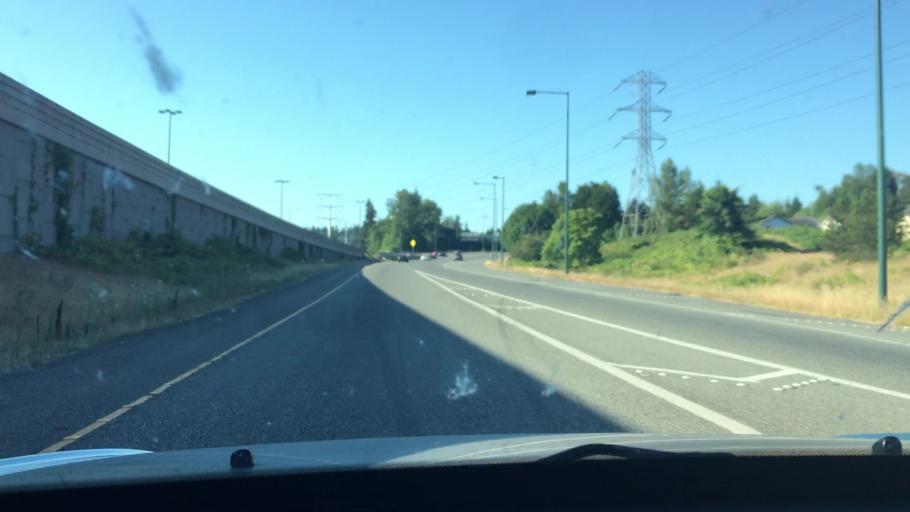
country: US
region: Washington
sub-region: King County
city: Newport
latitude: 47.5783
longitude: -122.1750
